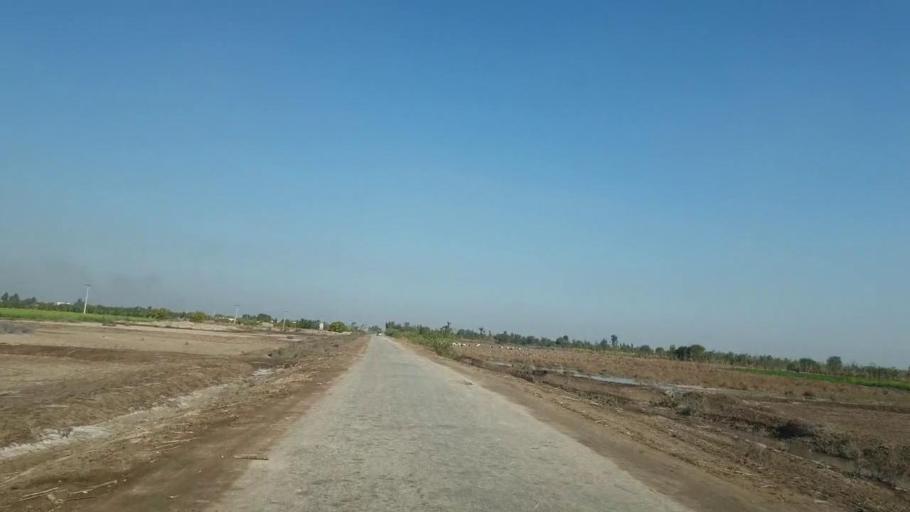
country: PK
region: Sindh
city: Mirpur Khas
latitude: 25.5735
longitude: 69.0462
